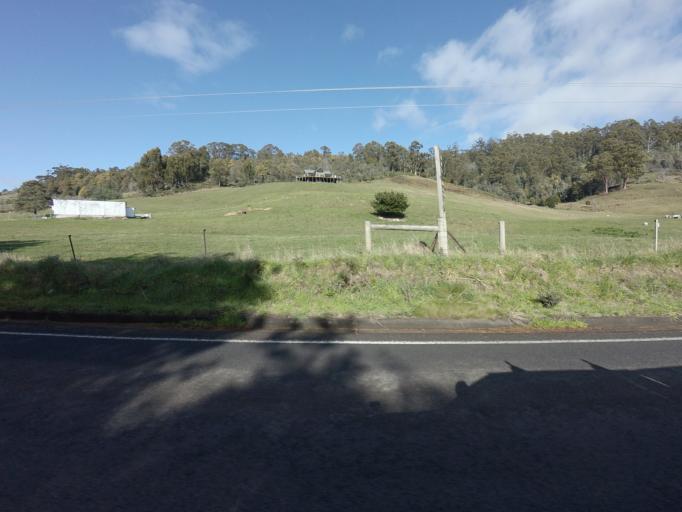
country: AU
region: Tasmania
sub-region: Huon Valley
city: Geeveston
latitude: -43.3046
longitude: 147.0083
